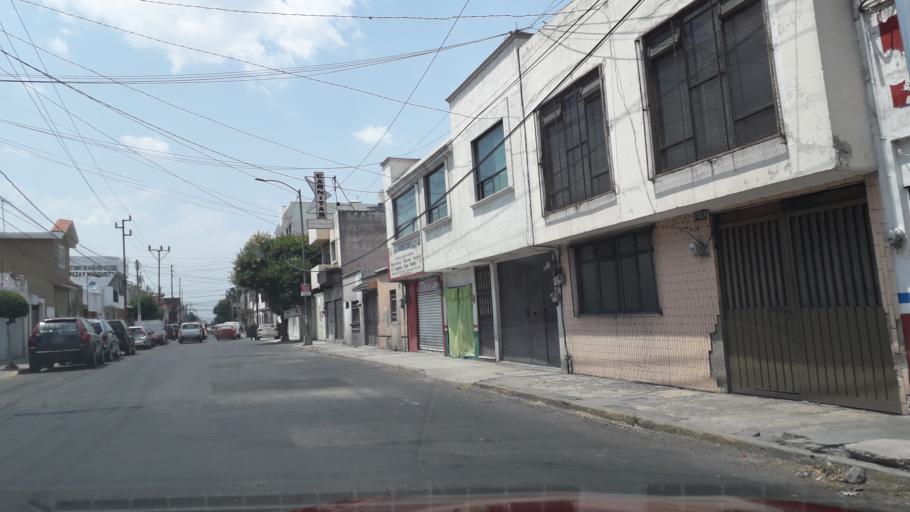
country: MX
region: Puebla
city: Puebla
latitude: 19.0421
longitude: -98.2153
